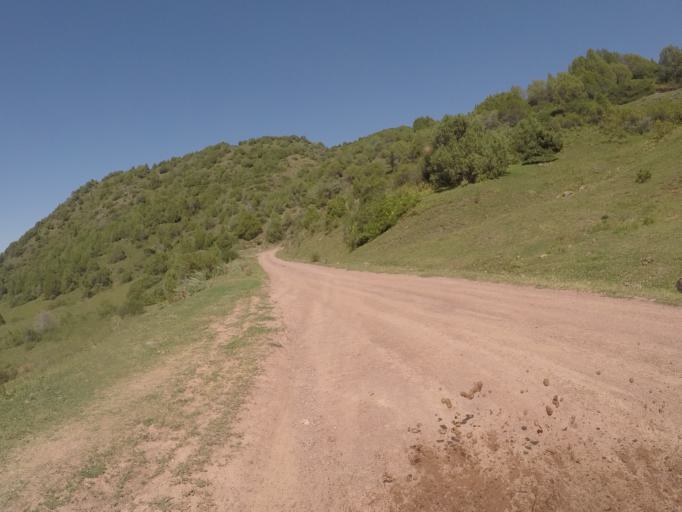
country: KG
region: Chuy
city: Bishkek
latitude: 42.6475
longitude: 74.5767
